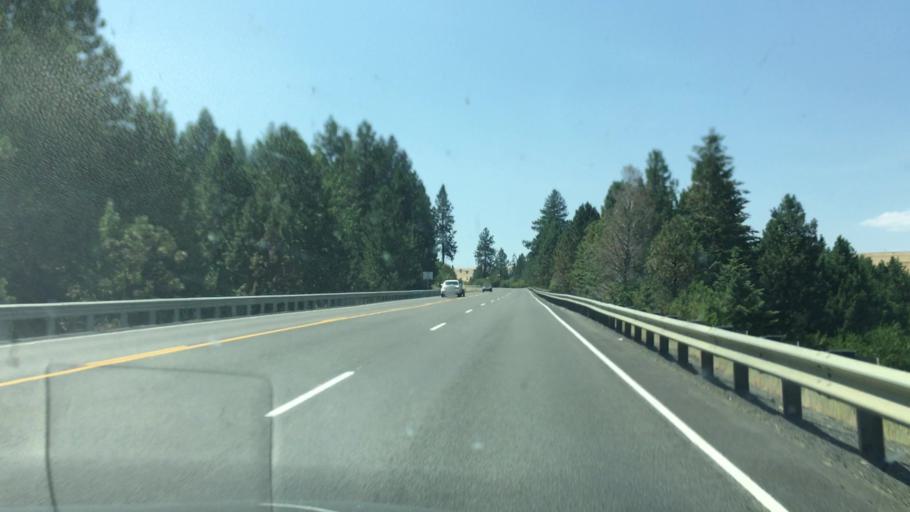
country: US
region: Idaho
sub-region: Idaho County
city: Grangeville
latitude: 45.8742
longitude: -116.2315
